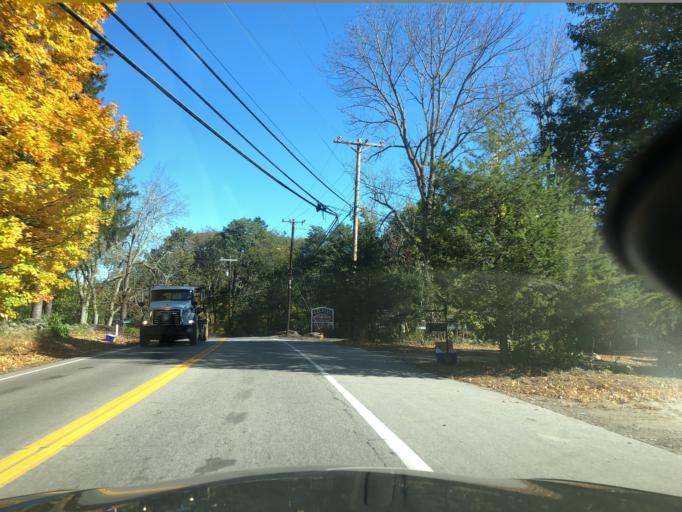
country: US
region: New Hampshire
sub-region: Rockingham County
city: Newmarket
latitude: 43.0627
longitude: -70.9370
